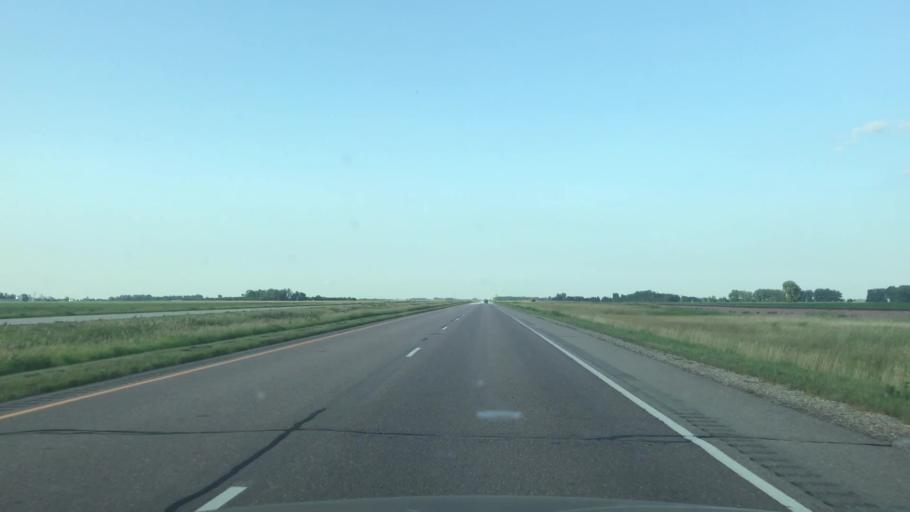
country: US
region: Minnesota
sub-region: Nobles County
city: Worthington
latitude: 43.7358
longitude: -95.4142
